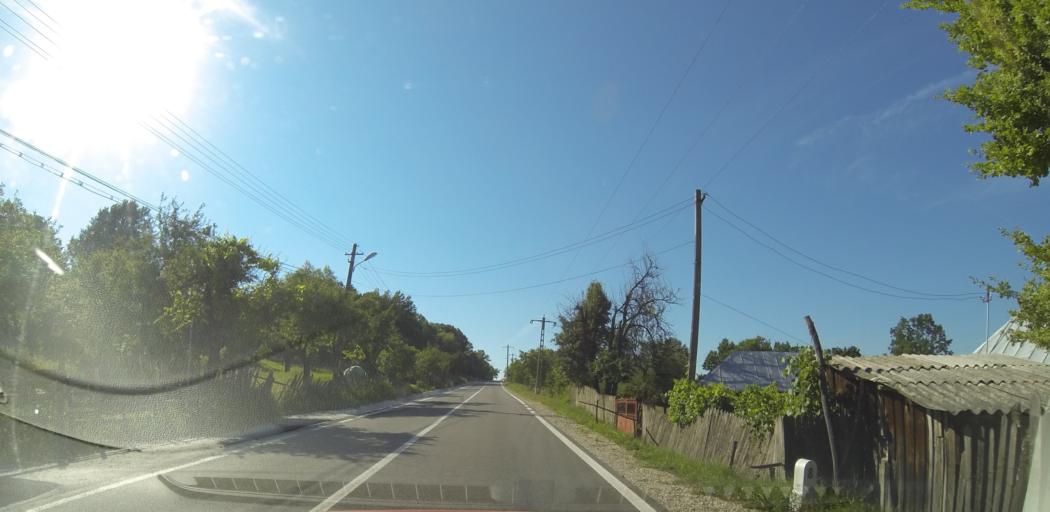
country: RO
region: Valcea
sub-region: Comuna Vaideeni
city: Vaideeni
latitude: 45.1696
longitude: 23.8852
